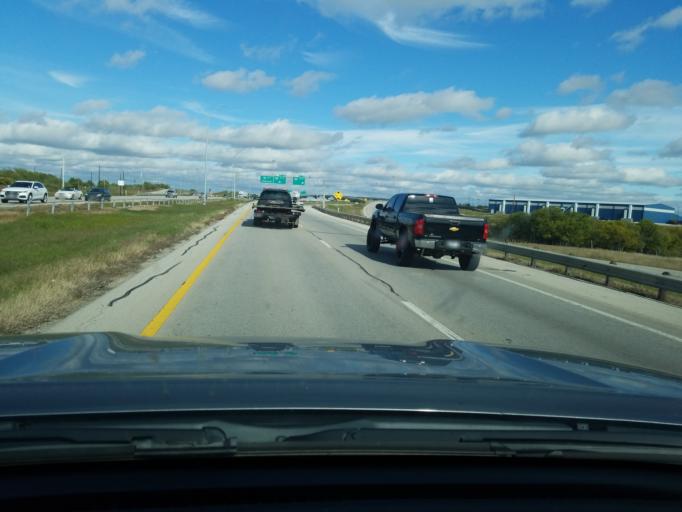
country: US
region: Texas
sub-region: Tarrant County
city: White Settlement
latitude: 32.7357
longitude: -97.4898
